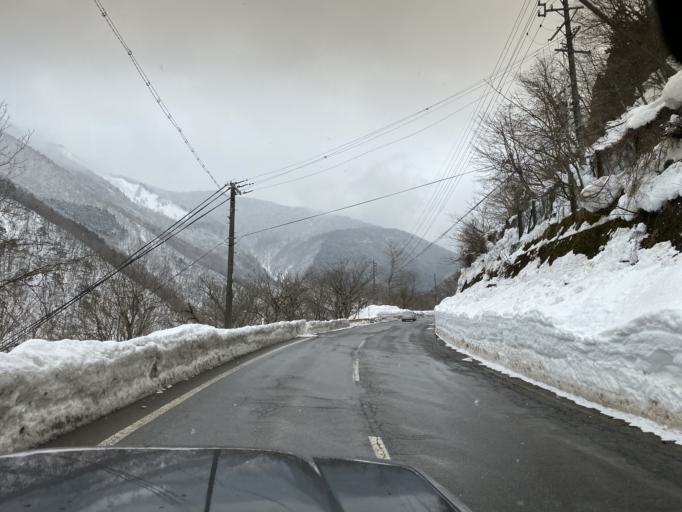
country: JP
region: Toyama
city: Fukumitsu
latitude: 36.2163
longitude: 136.8846
